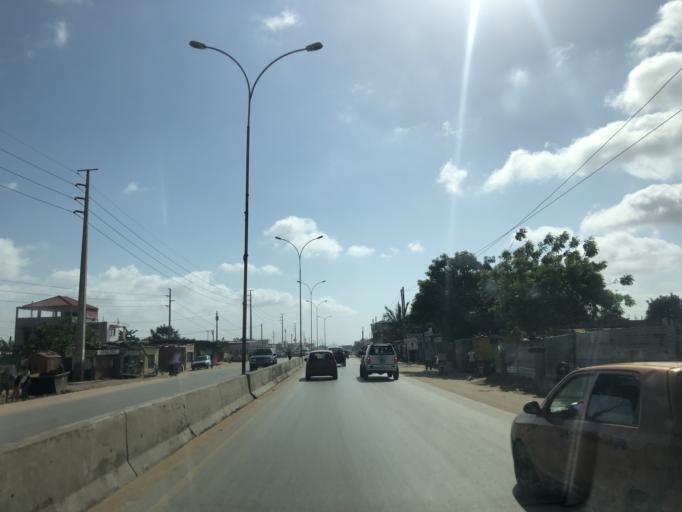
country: AO
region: Luanda
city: Luanda
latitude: -8.9035
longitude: 13.2483
